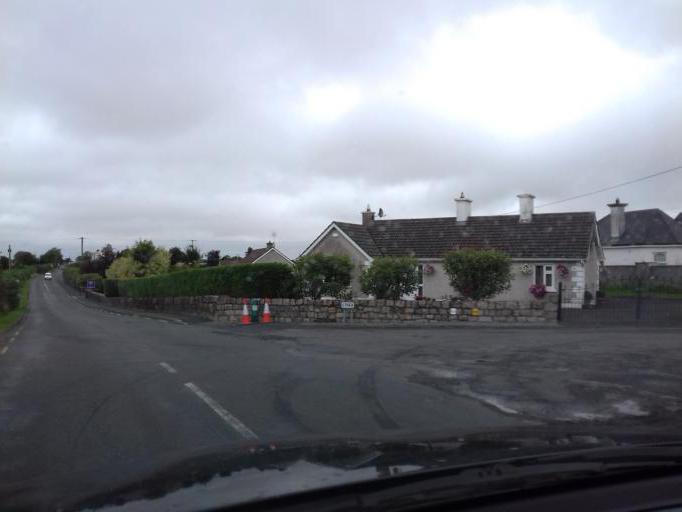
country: IE
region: Leinster
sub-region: County Carlow
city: Bagenalstown
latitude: 52.7294
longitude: -6.9711
